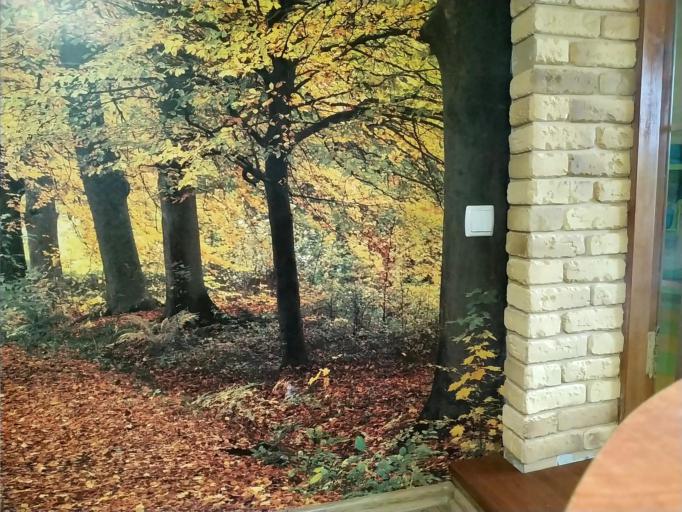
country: BY
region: Mogilev
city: Khotsimsk
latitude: 53.5548
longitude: 32.5228
